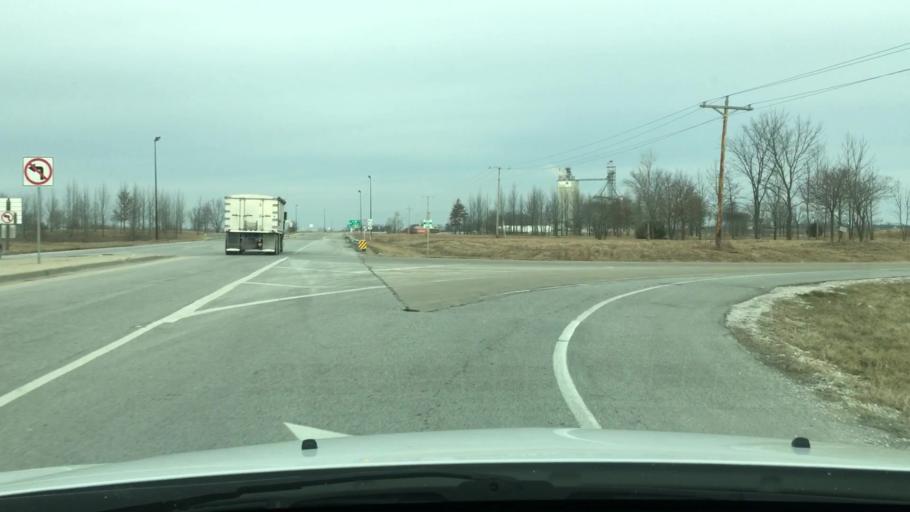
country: US
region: Illinois
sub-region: Pike County
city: Griggsville
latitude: 39.6725
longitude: -90.7688
